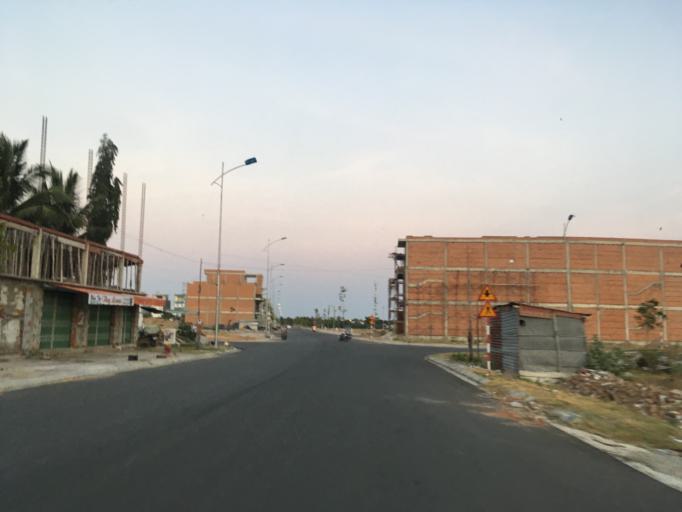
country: VN
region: Ninh Thuan
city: Phan Rang-Thap Cham
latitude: 11.5741
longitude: 108.9956
